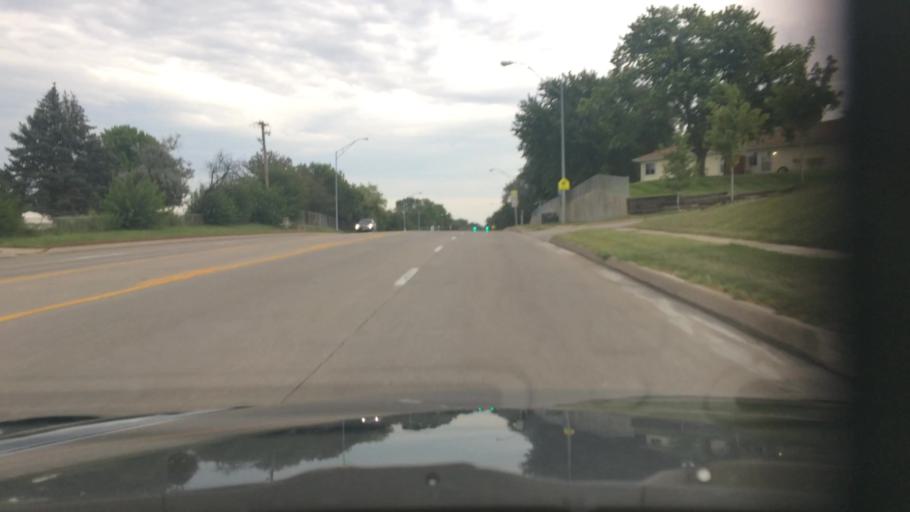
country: US
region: Nebraska
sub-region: Douglas County
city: Ralston
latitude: 41.2053
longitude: -96.0593
